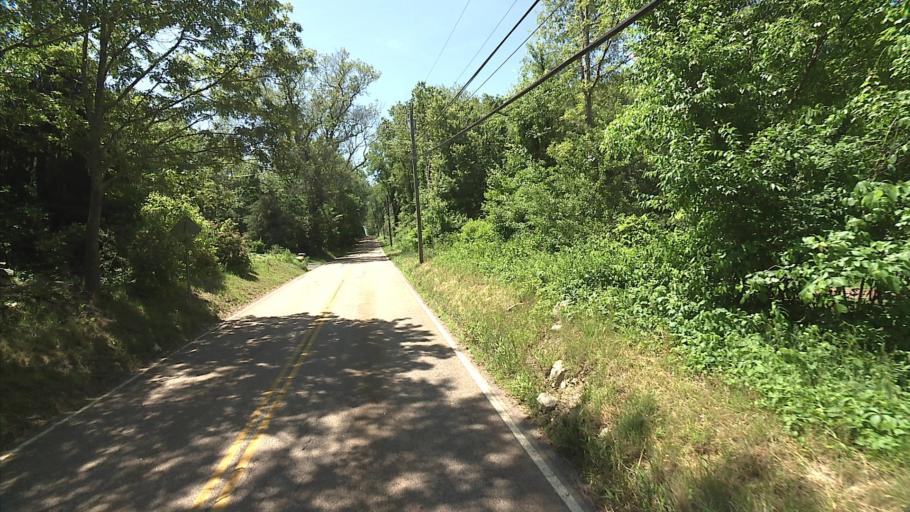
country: US
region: Rhode Island
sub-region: Washington County
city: Ashaway
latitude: 41.4499
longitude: -71.8461
